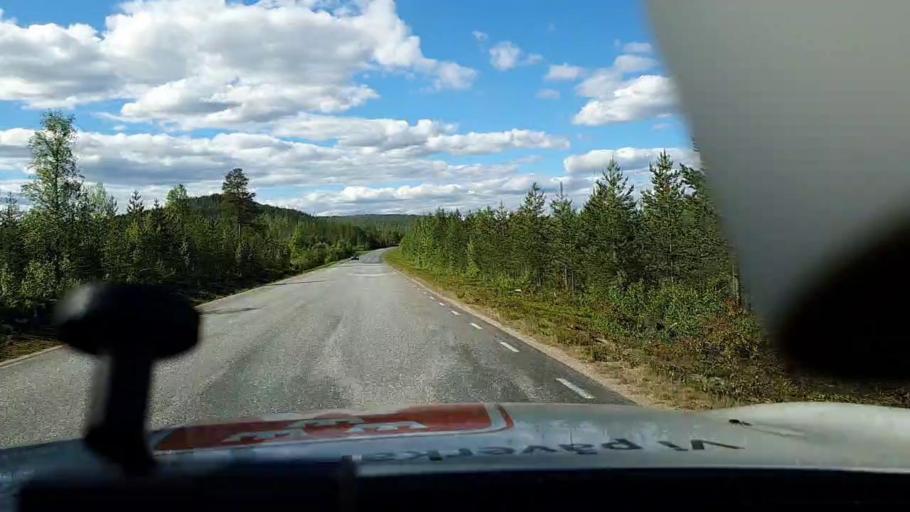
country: FI
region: Lapland
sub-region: Torniolaakso
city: Ylitornio
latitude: 66.3007
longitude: 23.6323
